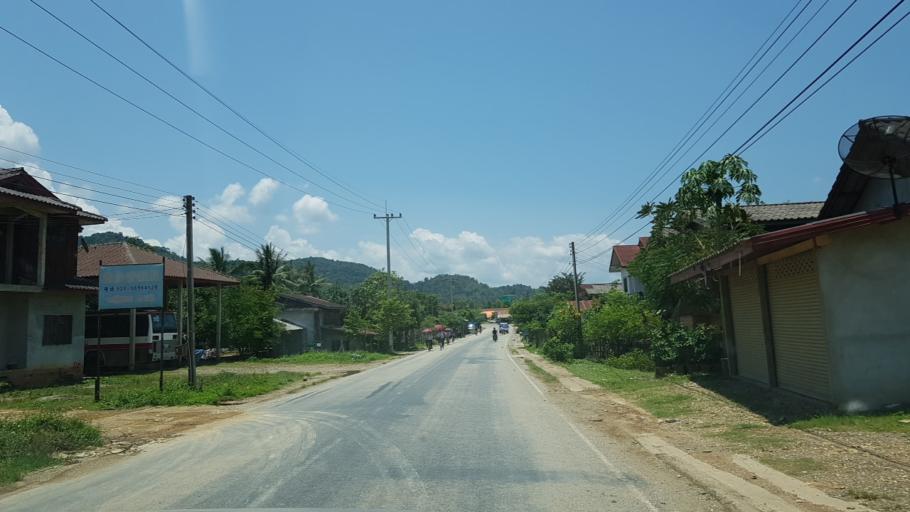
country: LA
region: Vientiane
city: Muang Kasi
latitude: 19.2284
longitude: 102.2524
